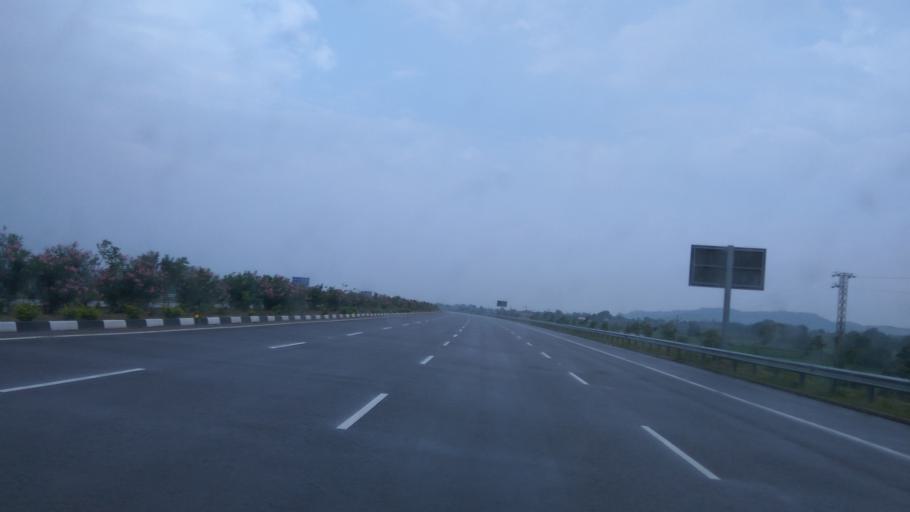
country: IN
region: Telangana
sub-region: Rangareddi
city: Ghatkesar
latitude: 17.4682
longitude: 78.6706
